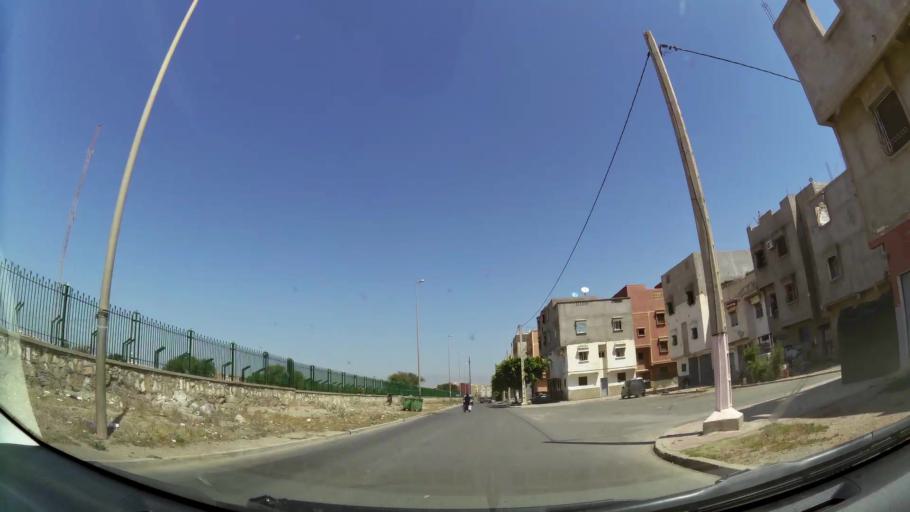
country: MA
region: Souss-Massa-Draa
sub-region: Inezgane-Ait Mellou
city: Inezgane
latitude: 30.3290
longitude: -9.5002
